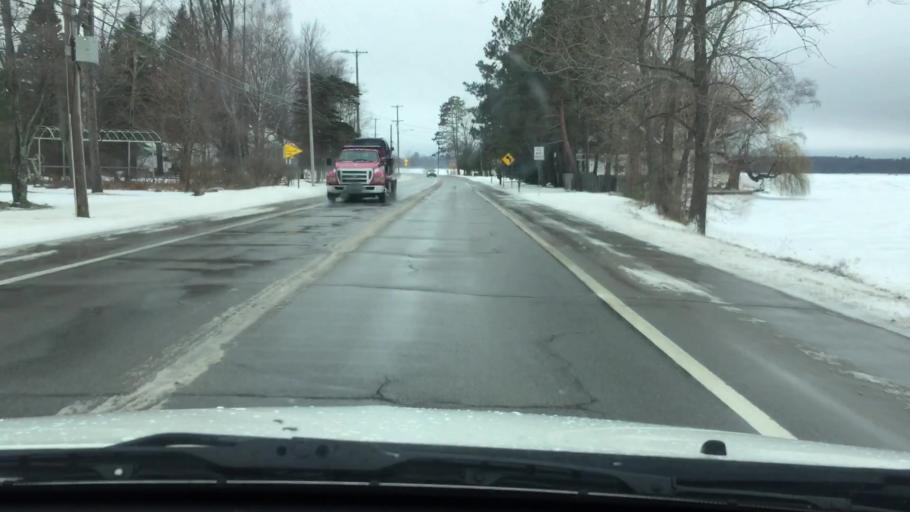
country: US
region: Michigan
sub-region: Wexford County
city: Cadillac
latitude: 44.2344
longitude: -85.4293
